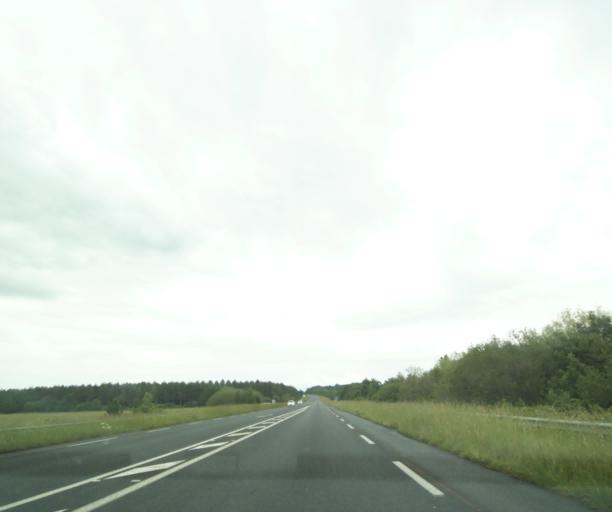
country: FR
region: Poitou-Charentes
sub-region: Departement des Deux-Sevres
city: Airvault
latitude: 46.7865
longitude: -0.2159
